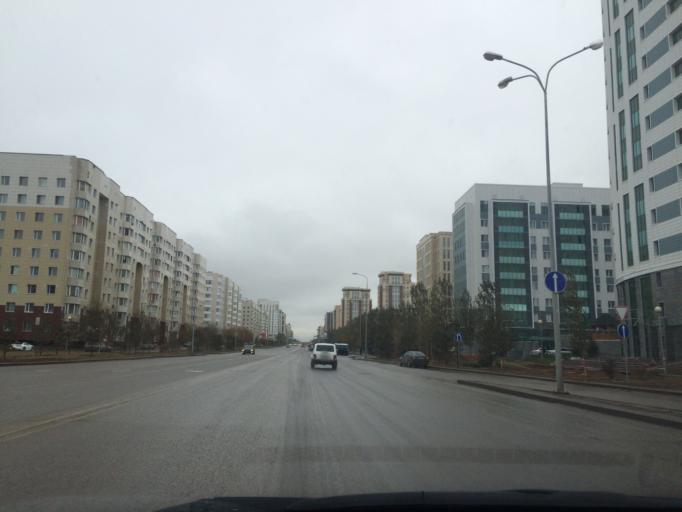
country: KZ
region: Astana Qalasy
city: Astana
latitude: 51.1160
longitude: 71.4121
